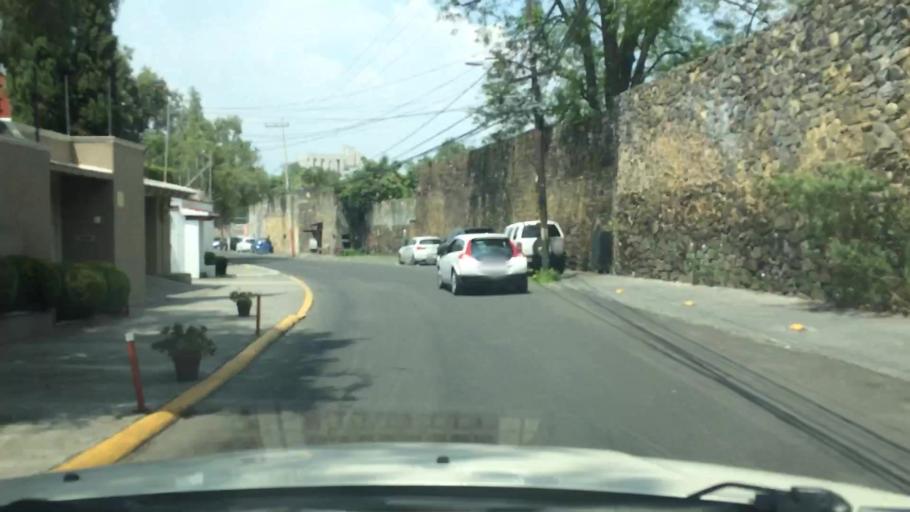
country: MX
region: Mexico City
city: Magdalena Contreras
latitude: 19.3279
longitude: -99.2050
